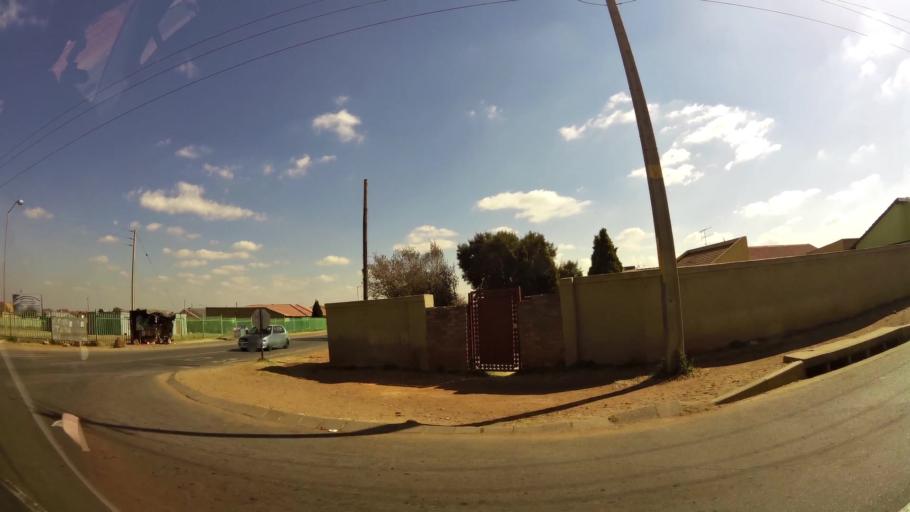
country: ZA
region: Gauteng
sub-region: West Rand District Municipality
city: Krugersdorp
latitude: -26.1519
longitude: 27.7817
